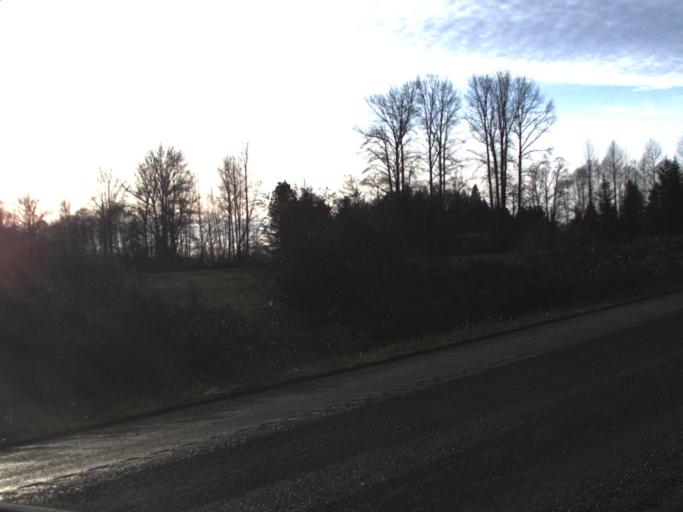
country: US
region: Washington
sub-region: Skagit County
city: Sedro-Woolley
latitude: 48.5309
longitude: -122.1466
